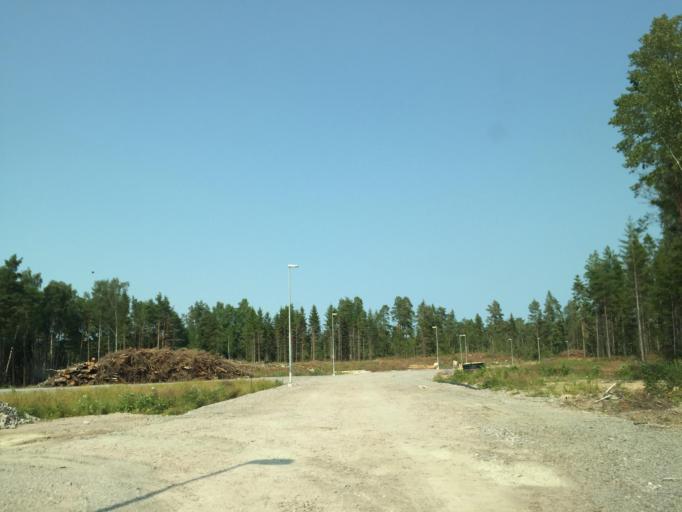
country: SE
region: Vaestra Goetaland
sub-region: Vanersborgs Kommun
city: Vanersborg
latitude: 58.3634
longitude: 12.2872
